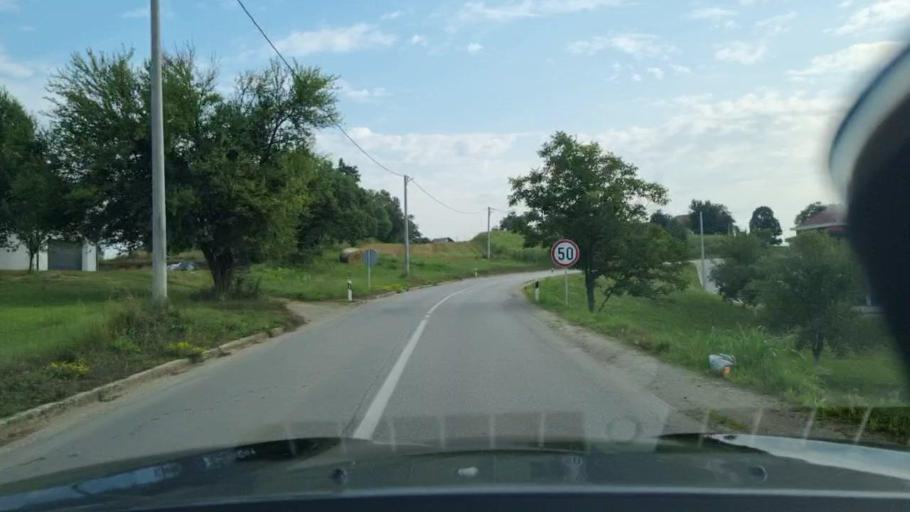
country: BA
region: Federation of Bosnia and Herzegovina
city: Podzvizd
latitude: 45.1726
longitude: 15.8713
